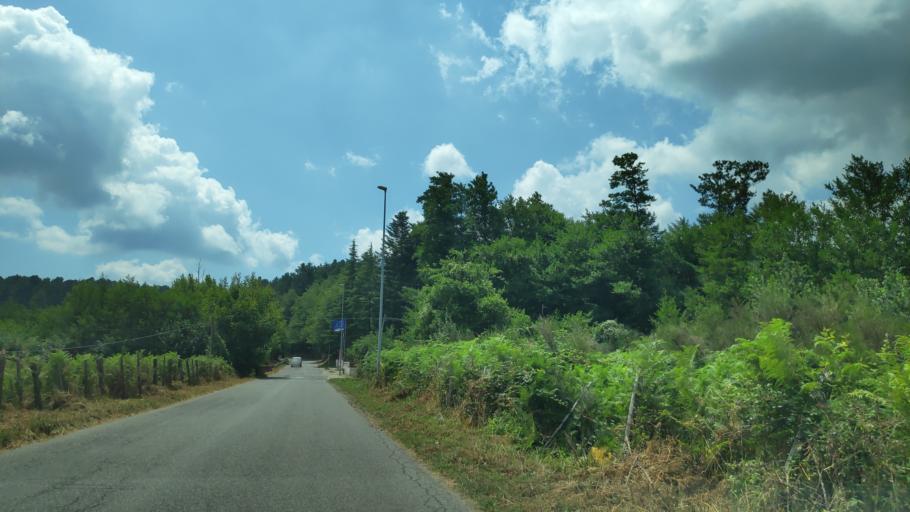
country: IT
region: Calabria
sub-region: Provincia di Vibo-Valentia
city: Mongiana
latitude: 38.5259
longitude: 16.3202
